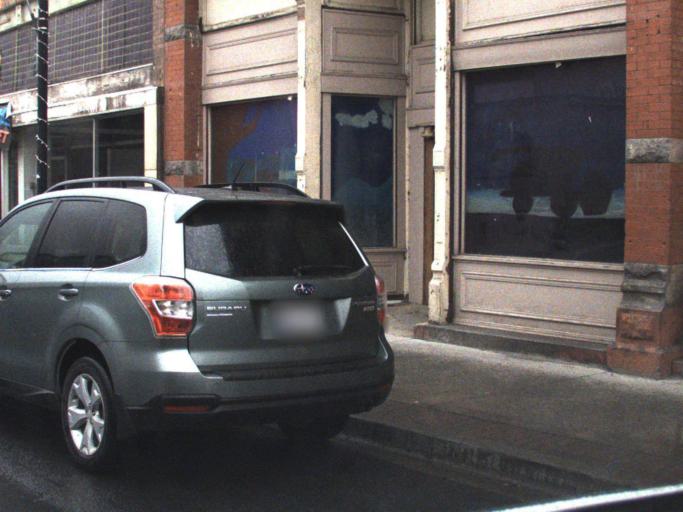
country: US
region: Washington
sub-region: Whitman County
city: Colfax
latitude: 46.8824
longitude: -117.3646
